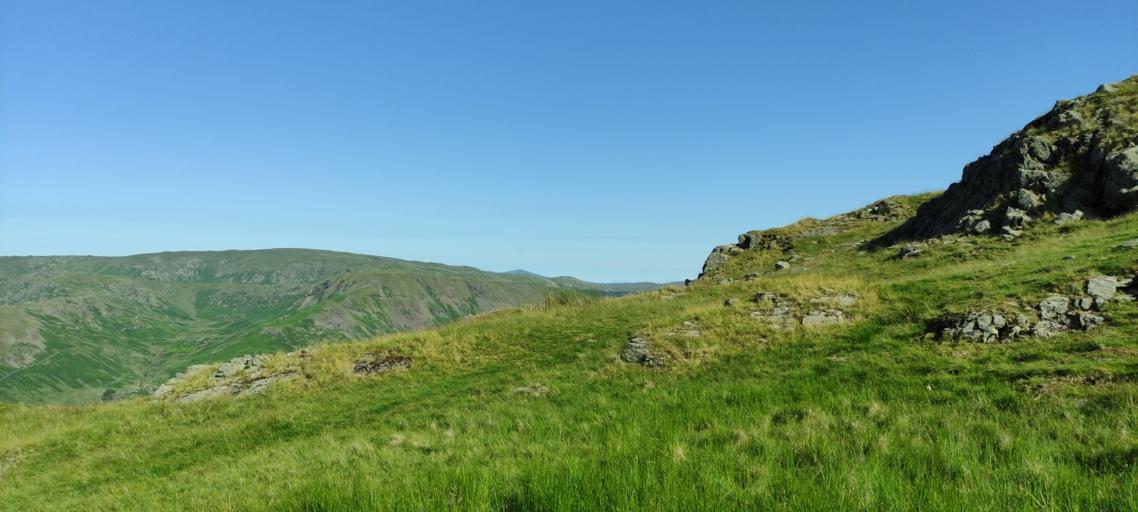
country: GB
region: England
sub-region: Cumbria
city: Ambleside
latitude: 54.4753
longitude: -3.0076
